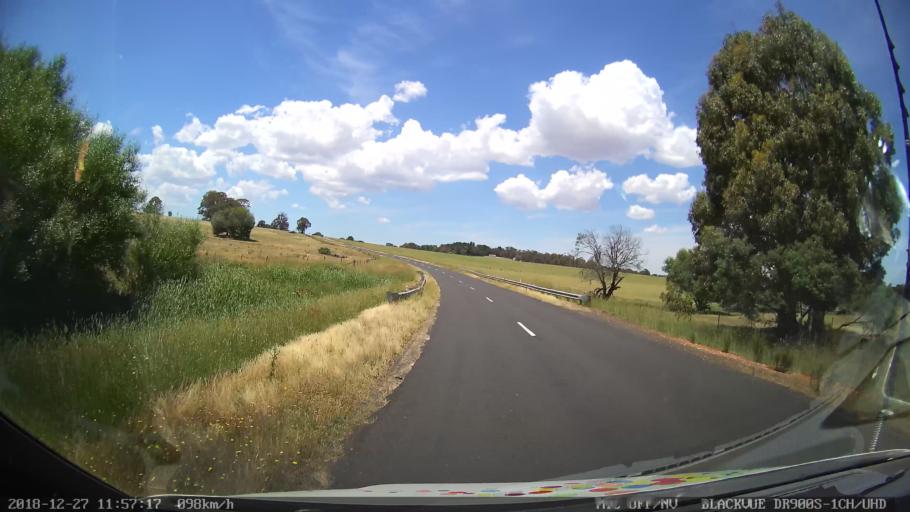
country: AU
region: New South Wales
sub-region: Blayney
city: Blayney
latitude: -33.7096
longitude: 149.3865
